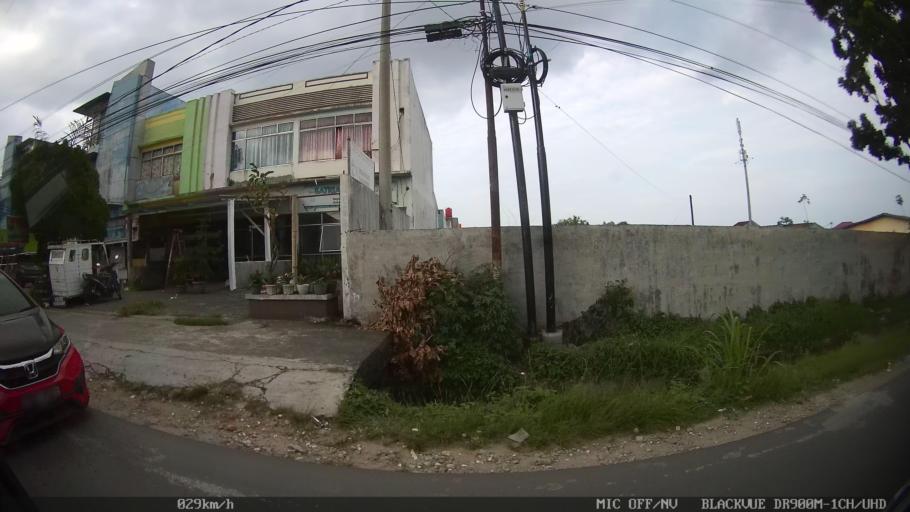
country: ID
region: North Sumatra
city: Sunggal
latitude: 3.5226
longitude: 98.6165
